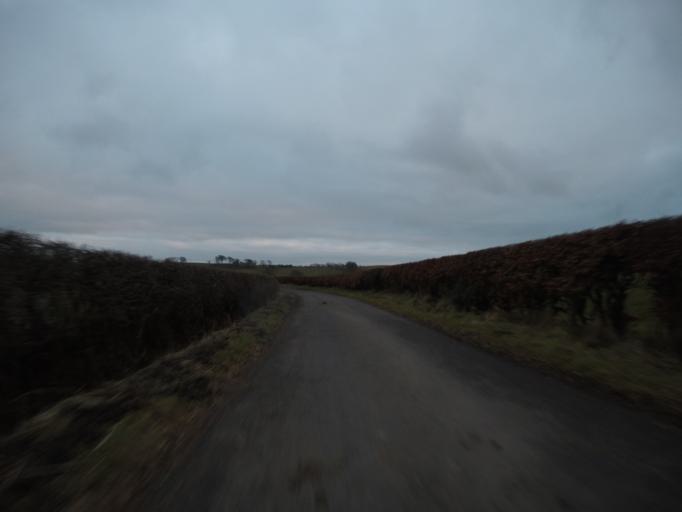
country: GB
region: Scotland
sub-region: North Ayrshire
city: Dalry
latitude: 55.6876
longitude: -4.7420
